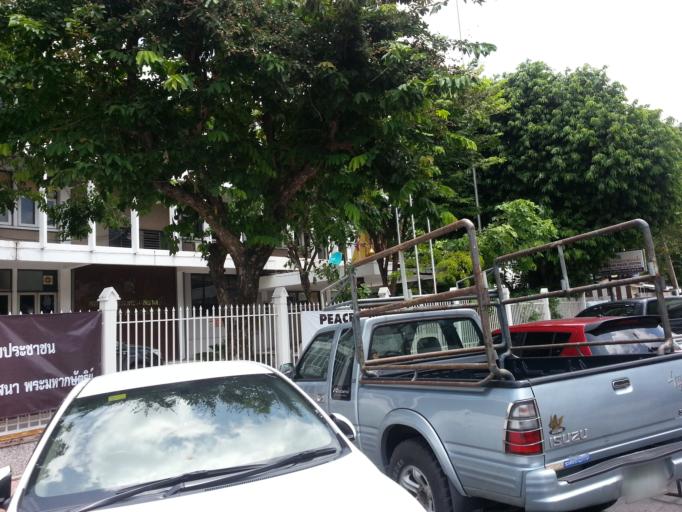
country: TH
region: Bangkok
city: Pom Prap Sattru Phai
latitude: 13.7578
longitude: 100.5077
